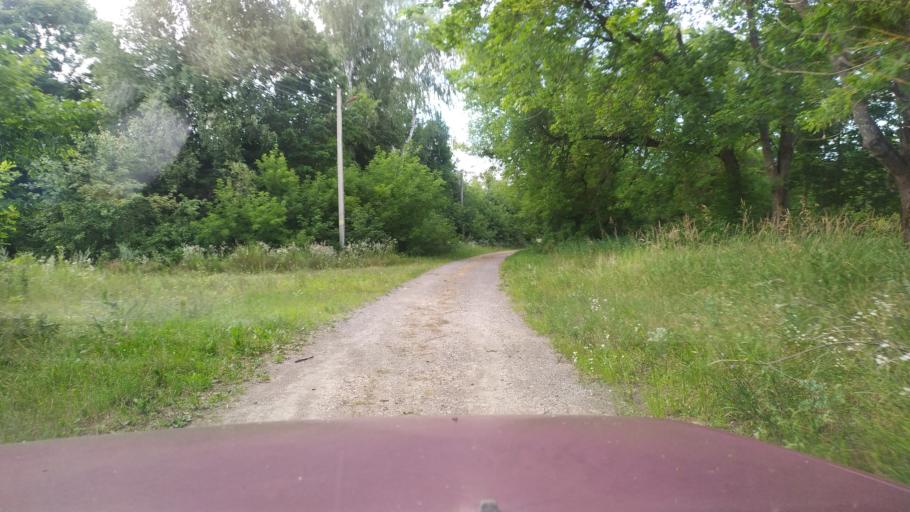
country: RU
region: Brjansk
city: Lyubovsho
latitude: 52.7477
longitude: 31.4606
